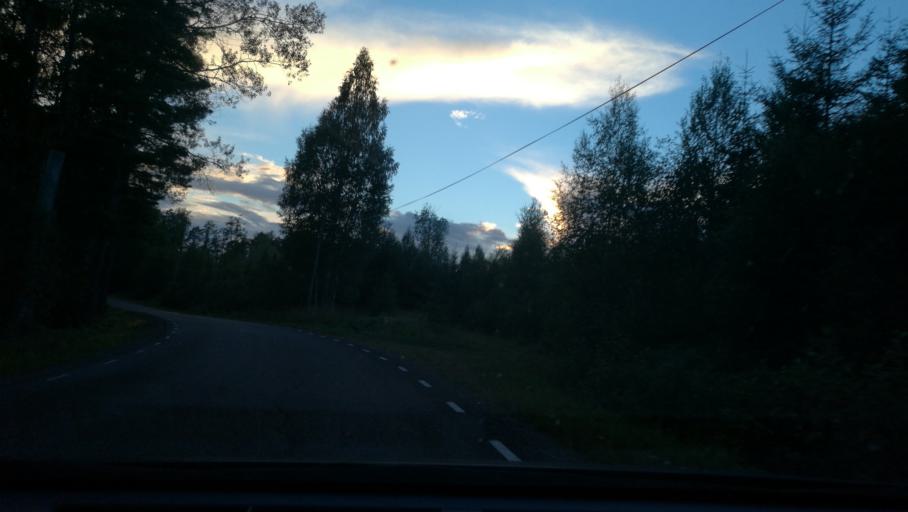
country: SE
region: OEstergoetland
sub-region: Norrkopings Kommun
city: Jursla
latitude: 58.8060
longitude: 16.1218
